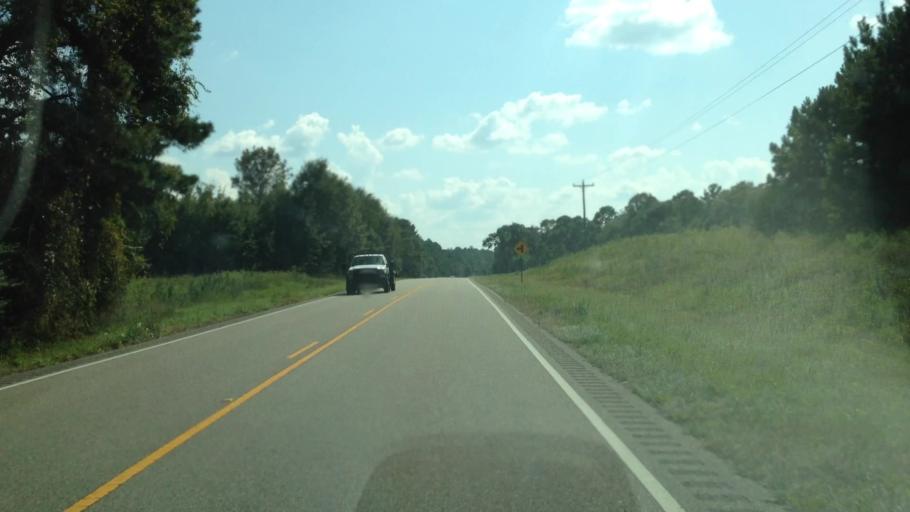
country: US
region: Alabama
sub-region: Covington County
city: Florala
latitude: 31.0609
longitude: -86.5756
